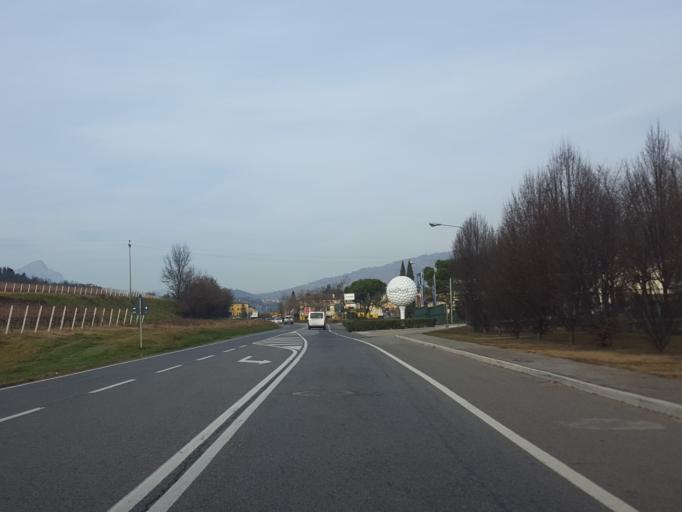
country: IT
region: Veneto
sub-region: Provincia di Verona
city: Costermano
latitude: 45.5828
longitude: 10.7525
